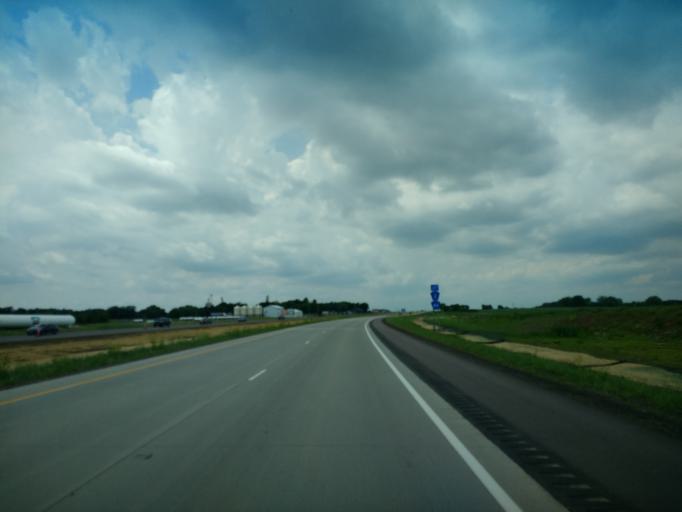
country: US
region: Minnesota
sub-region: Cottonwood County
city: Windom
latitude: 43.9104
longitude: -95.0320
